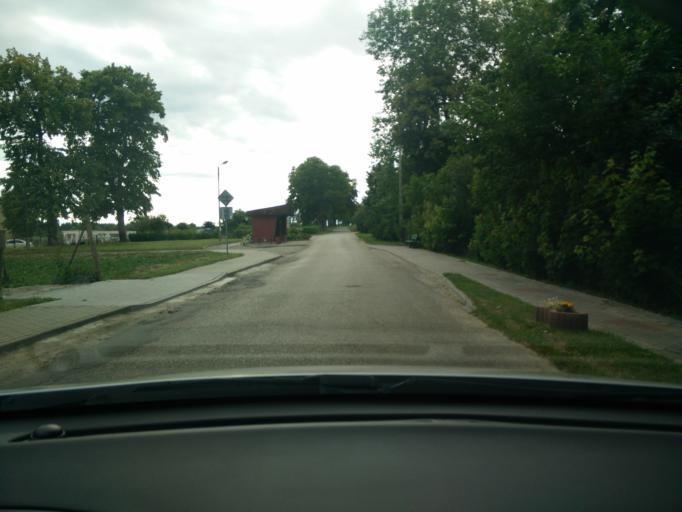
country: PL
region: Pomeranian Voivodeship
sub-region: Powiat pucki
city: Mrzezino
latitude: 54.6688
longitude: 18.4561
